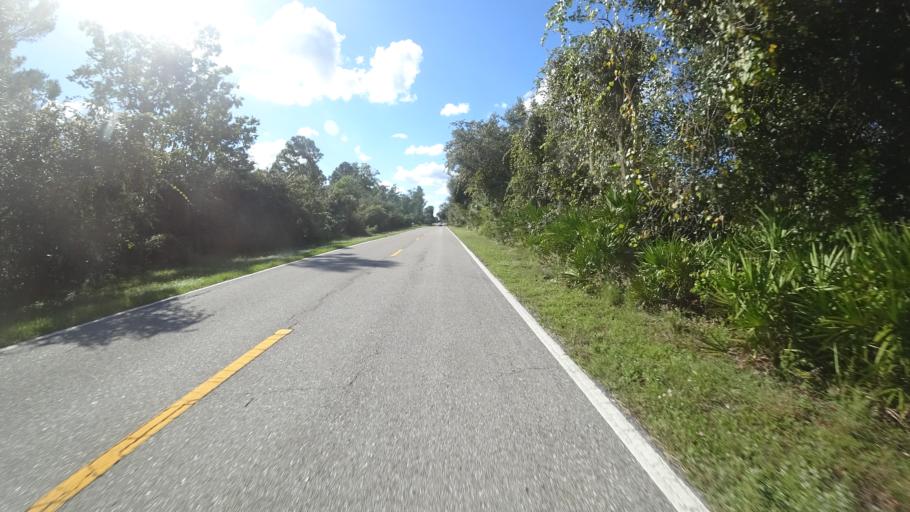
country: US
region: Florida
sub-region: Sarasota County
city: Lake Sarasota
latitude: 27.3058
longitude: -82.2630
